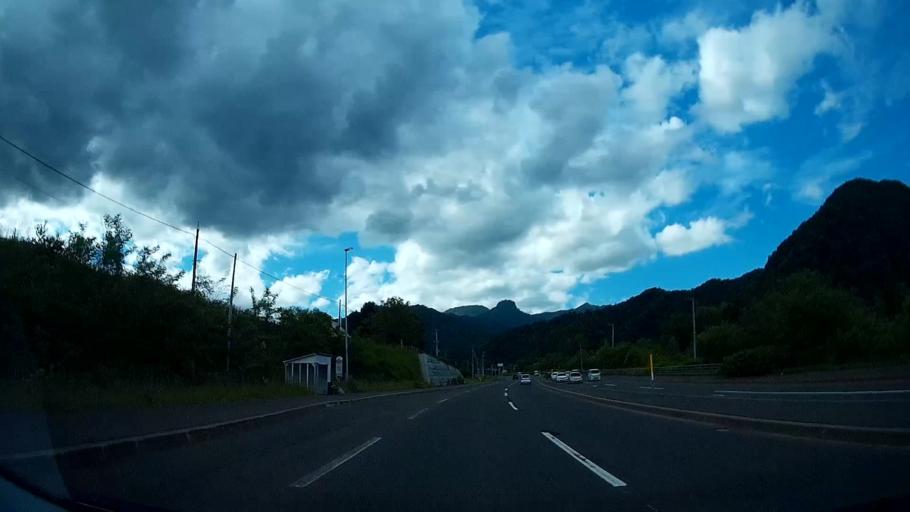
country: JP
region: Hokkaido
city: Sapporo
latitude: 42.9622
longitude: 141.2222
